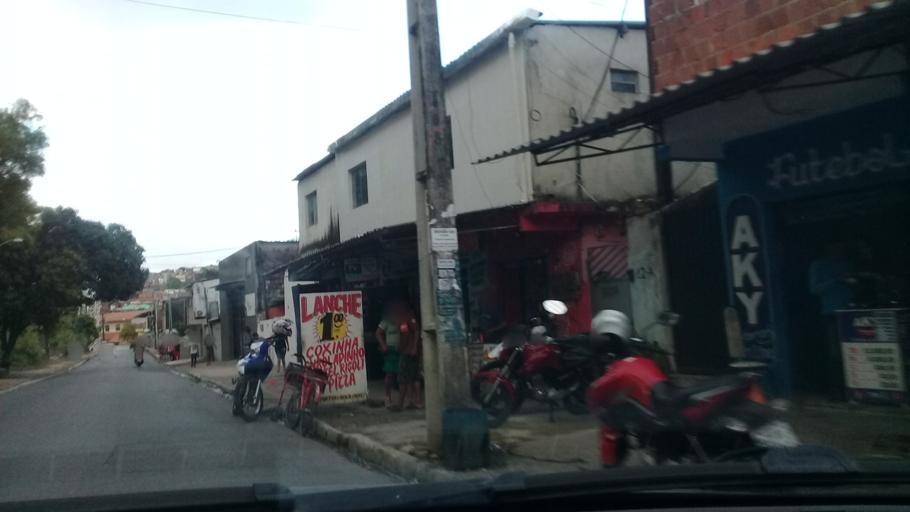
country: BR
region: Pernambuco
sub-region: Jaboatao Dos Guararapes
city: Jaboatao dos Guararapes
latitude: -8.1307
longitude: -34.9497
